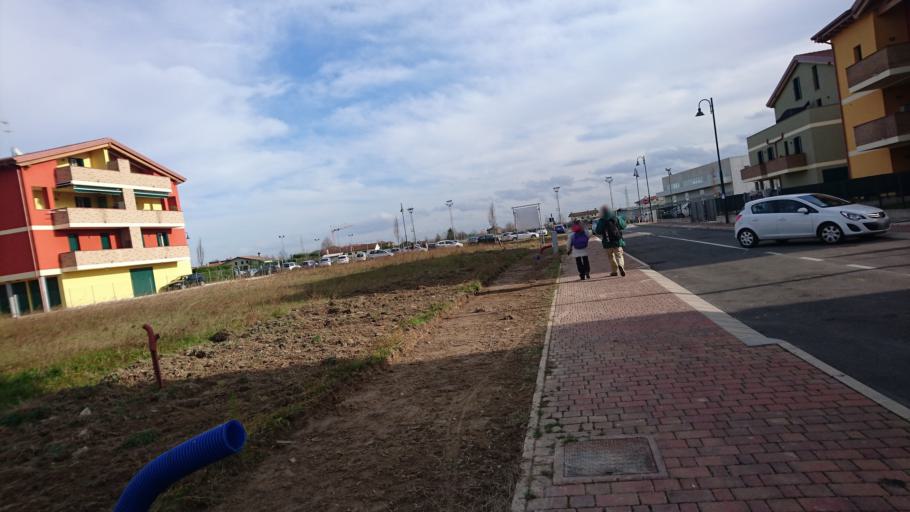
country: IT
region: Veneto
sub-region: Provincia di Padova
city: Polverara
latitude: 45.3076
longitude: 11.9561
